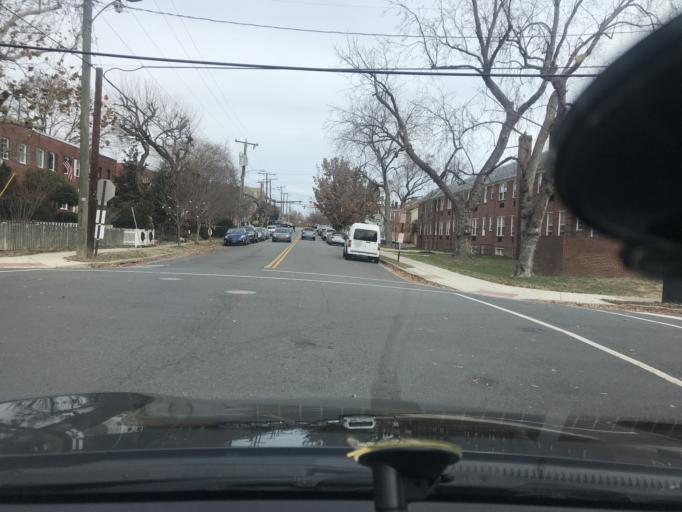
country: US
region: Virginia
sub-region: City of Alexandria
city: Alexandria
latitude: 38.7971
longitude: -77.0498
